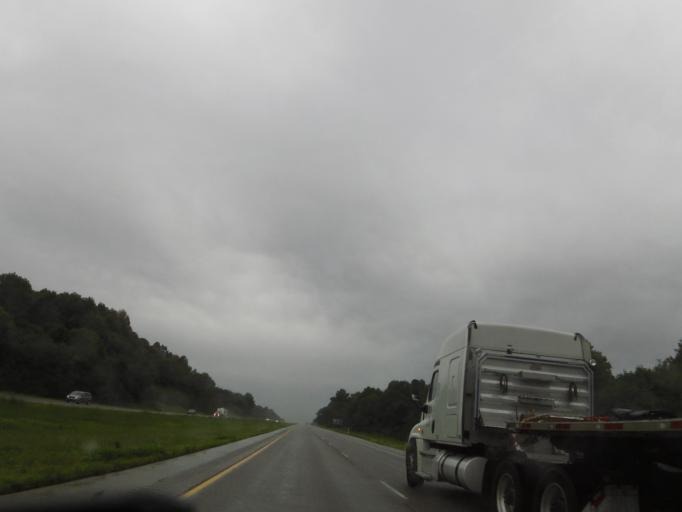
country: US
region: Illinois
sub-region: Johnson County
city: Vienna
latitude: 37.3953
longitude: -88.8445
